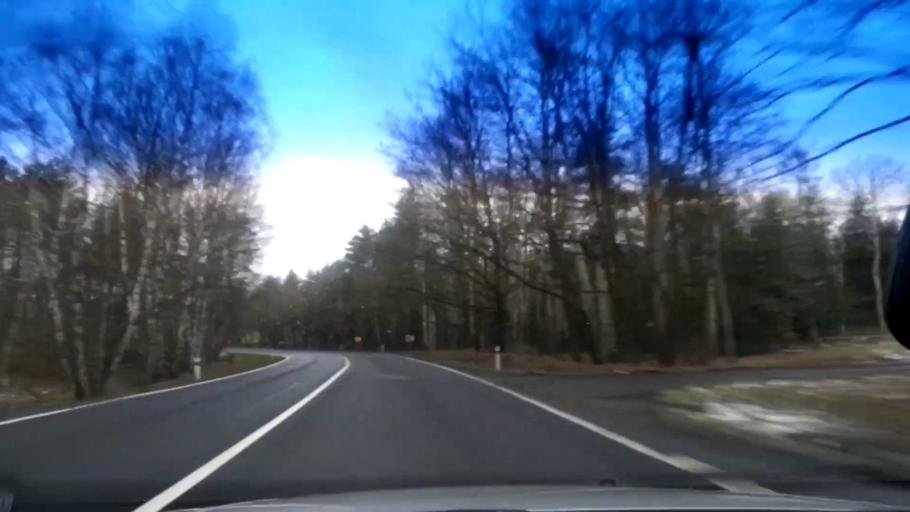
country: CZ
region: Karlovarsky
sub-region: Okres Cheb
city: Frantiskovy Lazne
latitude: 50.1382
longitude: 12.3198
